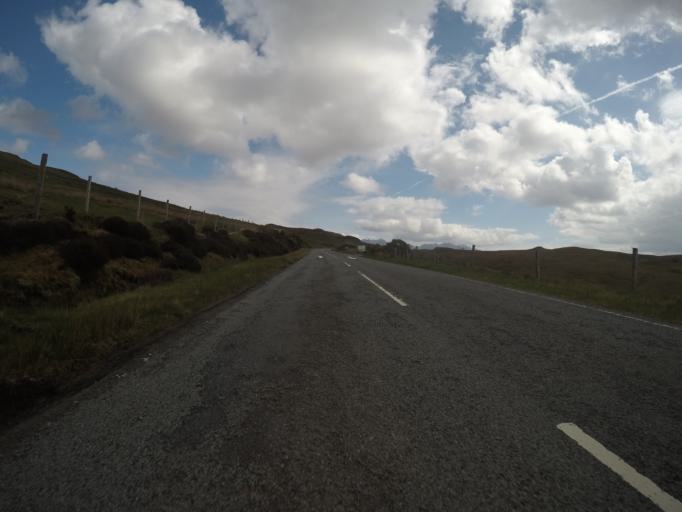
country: GB
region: Scotland
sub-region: Highland
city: Isle of Skye
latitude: 57.3213
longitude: -6.3270
